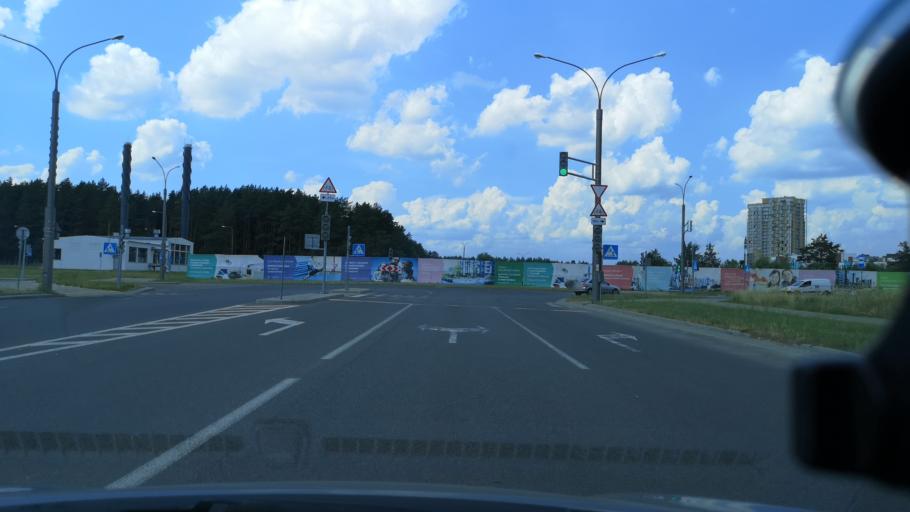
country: BY
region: Minsk
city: Borovlyany
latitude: 53.9499
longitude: 27.6625
